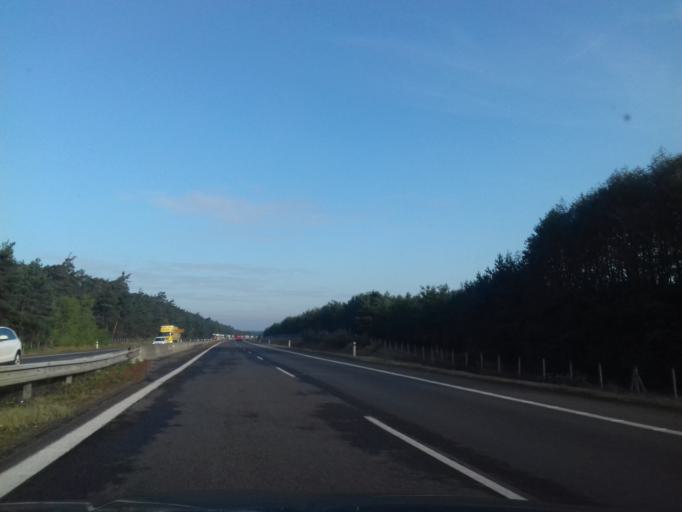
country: SK
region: Bratislavsky
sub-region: Okres Malacky
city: Malacky
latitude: 48.3743
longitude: 17.0204
